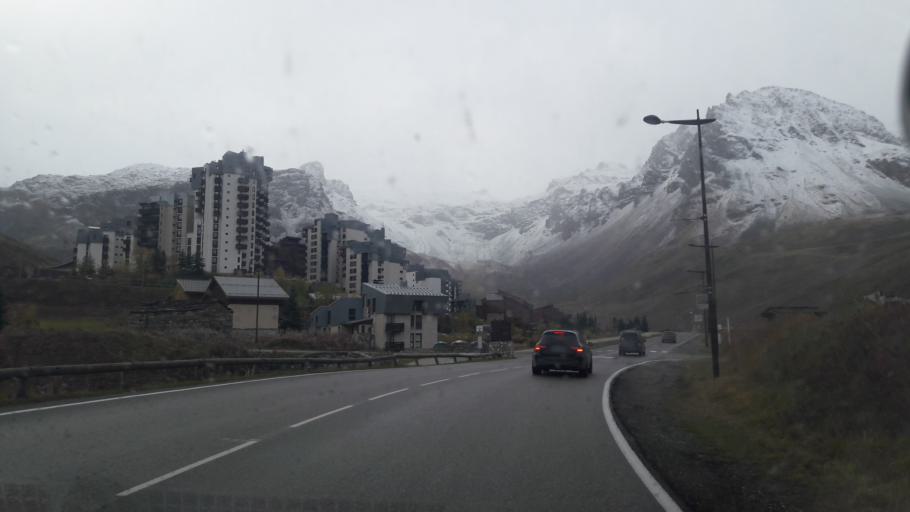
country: FR
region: Rhone-Alpes
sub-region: Departement de la Savoie
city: Tignes
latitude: 45.4609
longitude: 6.9005
